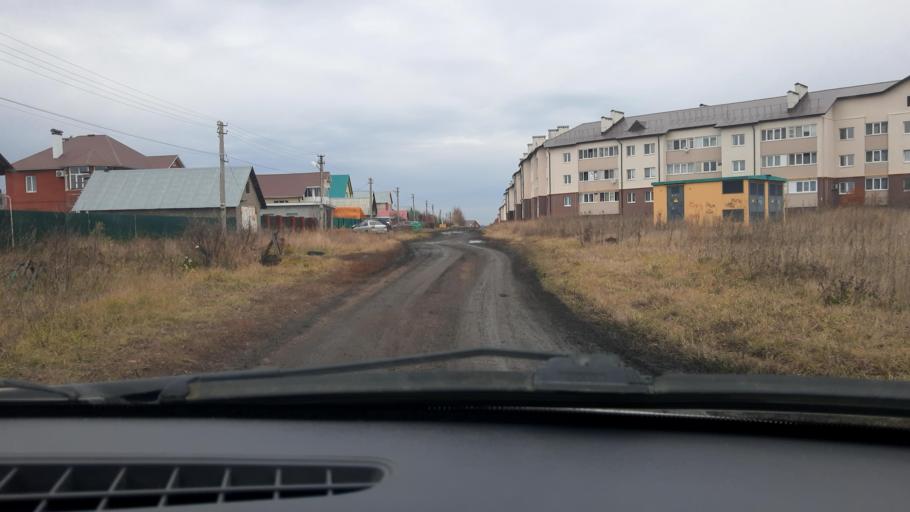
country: RU
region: Bashkortostan
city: Avdon
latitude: 54.6950
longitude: 55.8017
